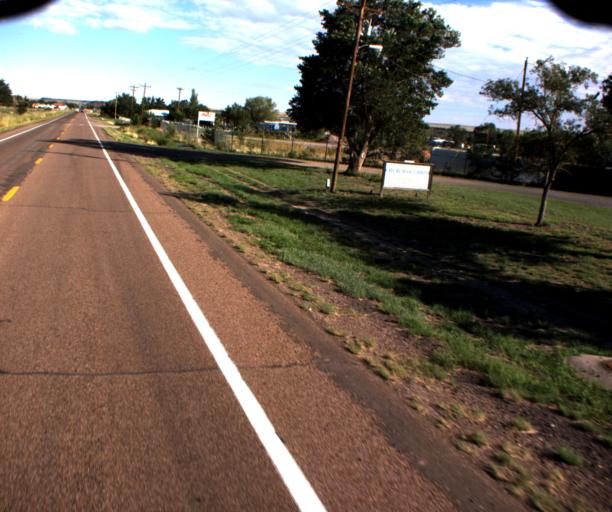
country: US
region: Arizona
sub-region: Apache County
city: Springerville
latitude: 34.1169
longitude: -109.2563
